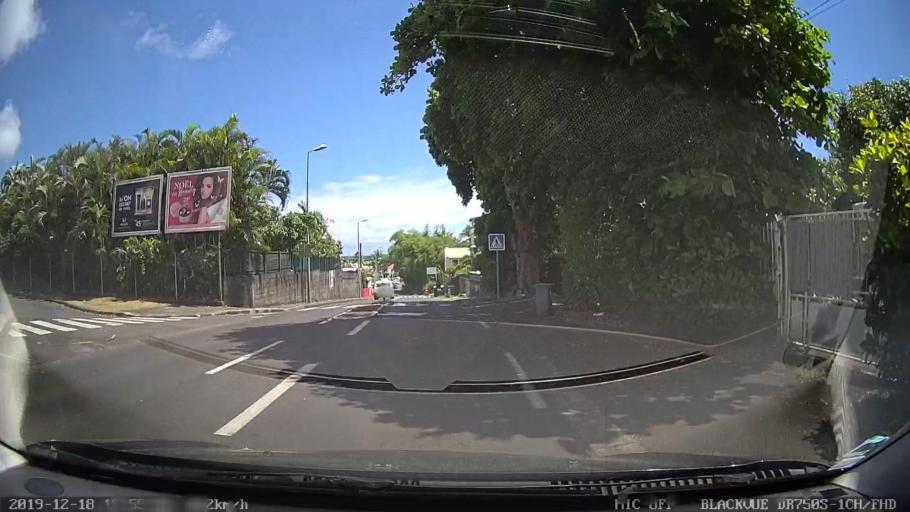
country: RE
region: Reunion
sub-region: Reunion
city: Saint-Andre
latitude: -20.9330
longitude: 55.6383
